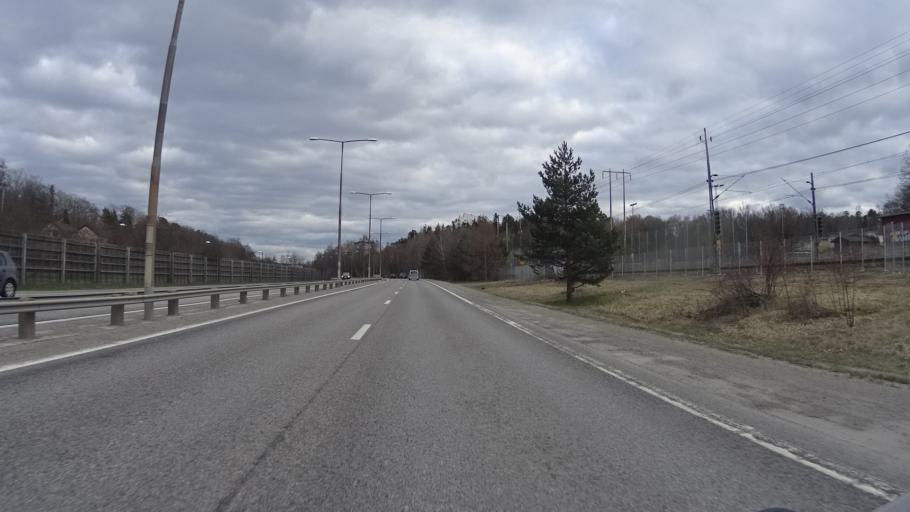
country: SE
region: Stockholm
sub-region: Stockholms Kommun
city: Arsta
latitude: 59.2655
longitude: 18.0237
